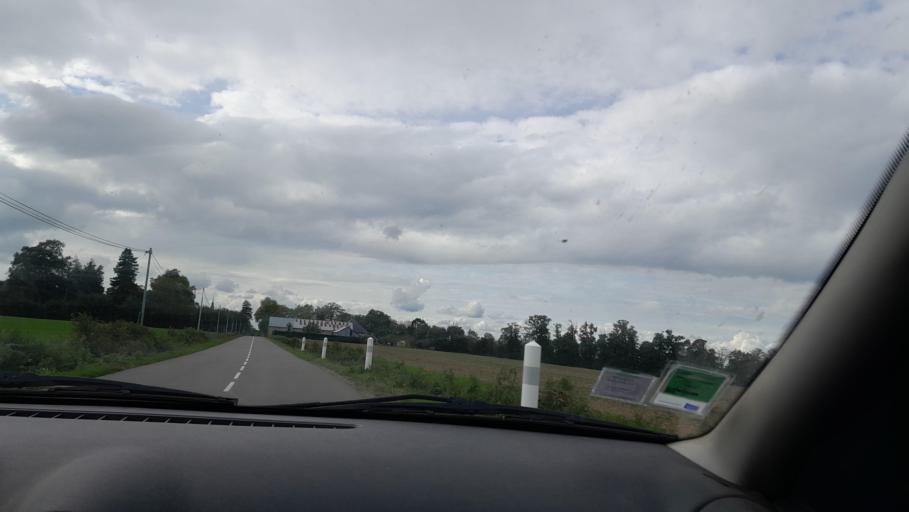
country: FR
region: Brittany
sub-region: Departement d'Ille-et-Vilaine
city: Argentre-du-Plessis
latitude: 48.0508
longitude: -1.0959
